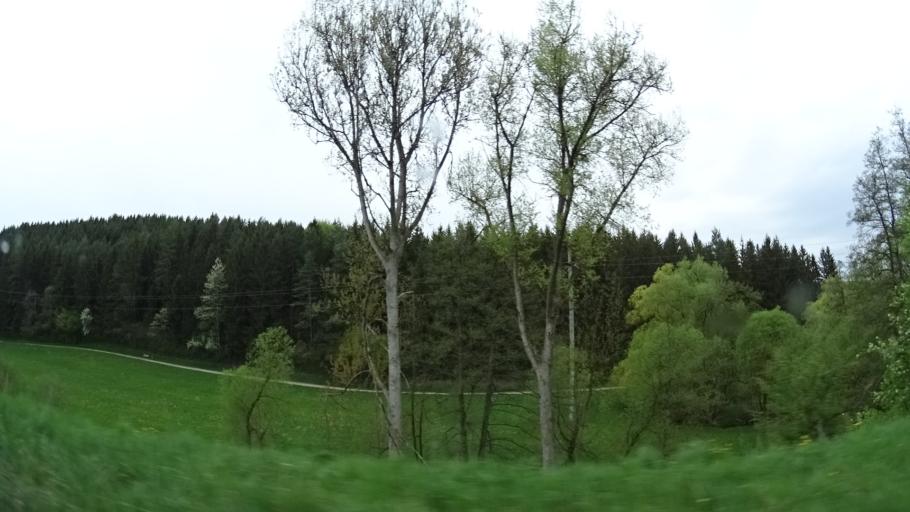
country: DE
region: Baden-Wuerttemberg
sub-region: Freiburg Region
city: Niedereschach
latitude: 48.1222
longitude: 8.5215
